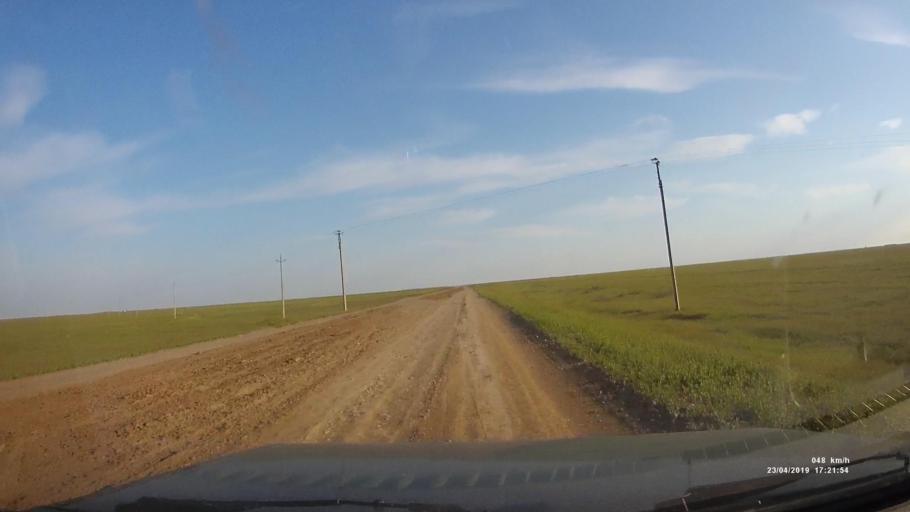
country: RU
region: Kalmykiya
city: Priyutnoye
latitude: 46.1725
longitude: 43.5059
